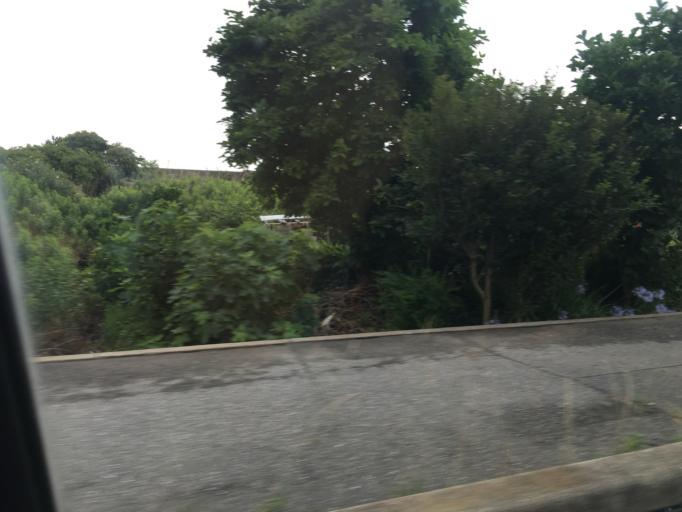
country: JP
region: Aichi
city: Ishiki
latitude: 34.7969
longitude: 137.0162
